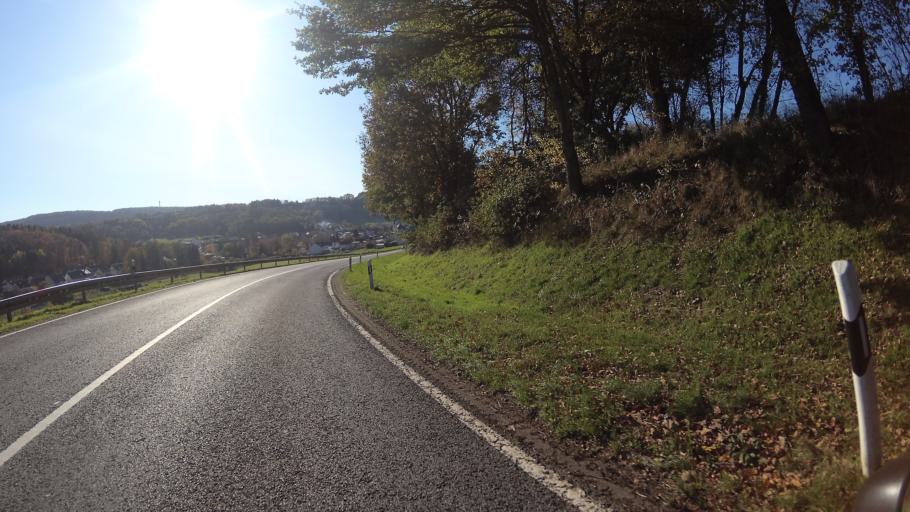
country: DE
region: Saarland
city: Losheim
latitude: 49.4826
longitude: 6.7101
